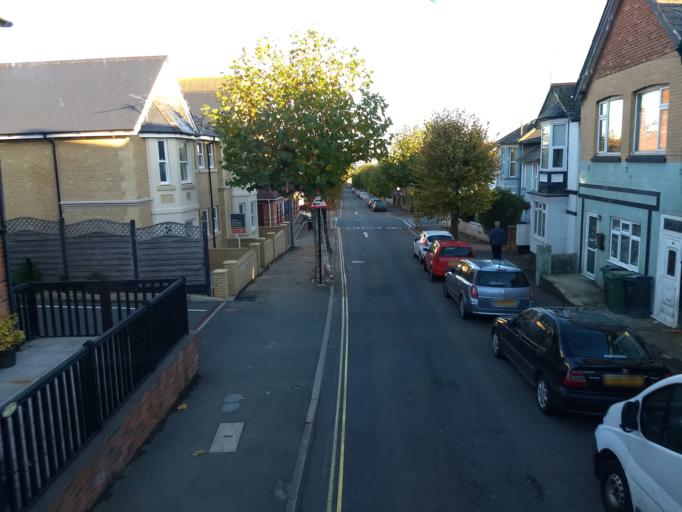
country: GB
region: England
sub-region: Isle of Wight
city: Sandown
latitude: 50.6561
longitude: -1.1556
